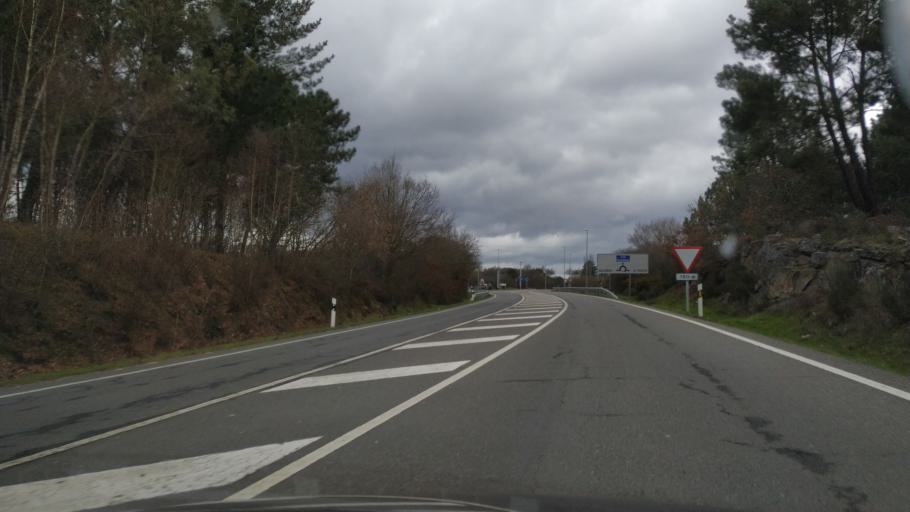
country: ES
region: Galicia
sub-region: Provincia de Ourense
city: Allariz
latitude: 42.2013
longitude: -7.8068
